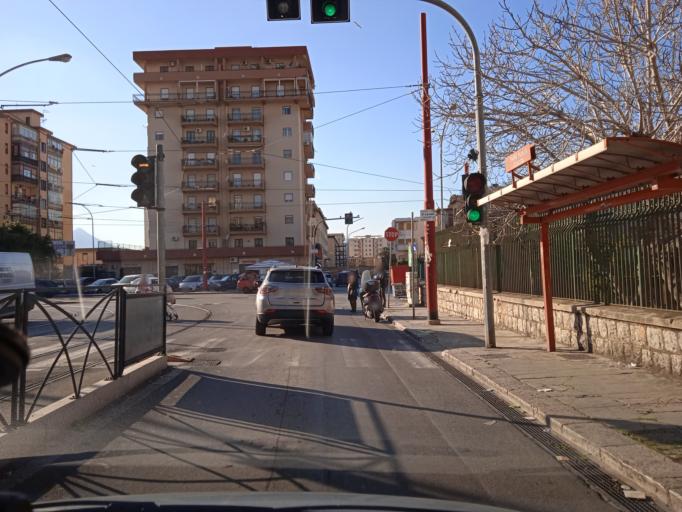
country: IT
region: Sicily
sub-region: Palermo
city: Ciaculli
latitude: 38.1035
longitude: 13.3868
